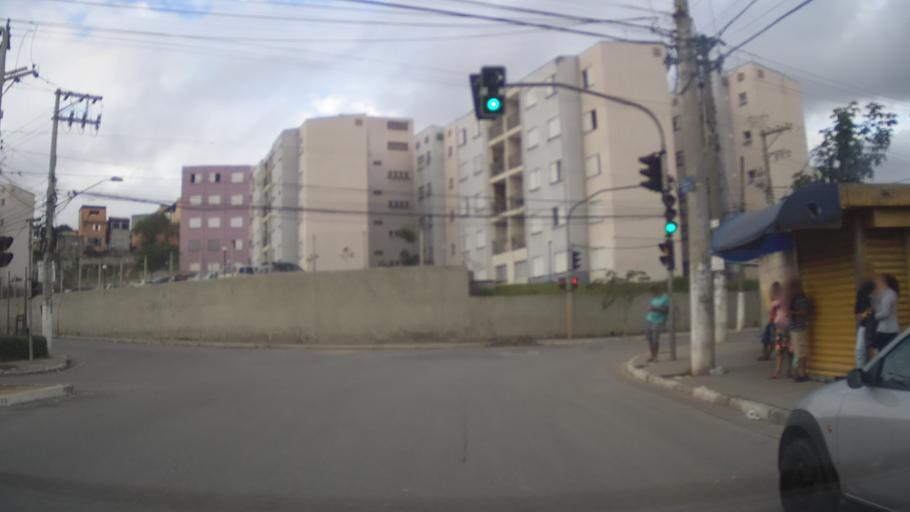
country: BR
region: Sao Paulo
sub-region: Itaquaquecetuba
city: Itaquaquecetuba
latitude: -23.4631
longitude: -46.3947
